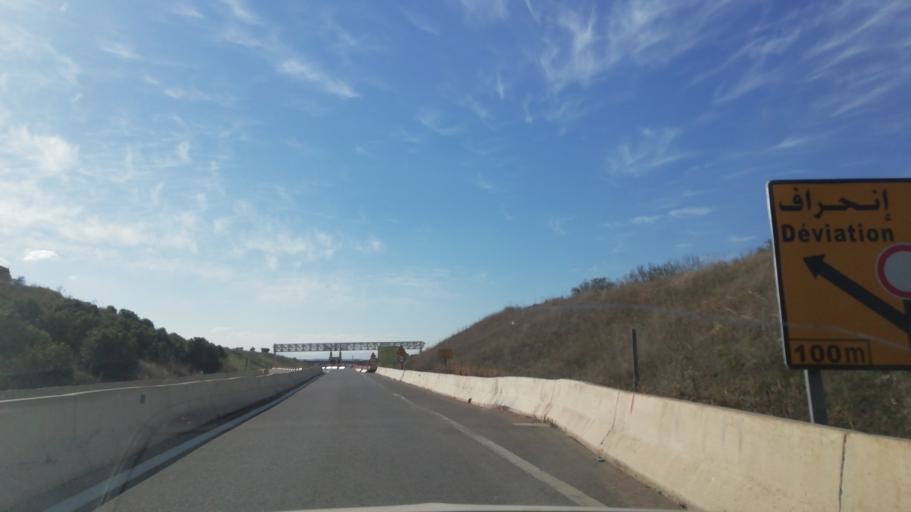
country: DZ
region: Tlemcen
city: Bensekrane
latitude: 34.9851
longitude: -1.2163
